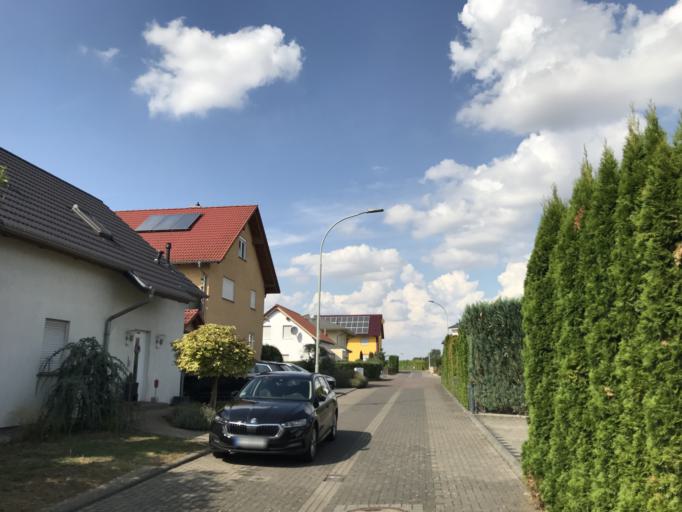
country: DE
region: Hesse
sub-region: Regierungsbezirk Darmstadt
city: Wolfersheim
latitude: 50.3749
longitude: 8.8116
